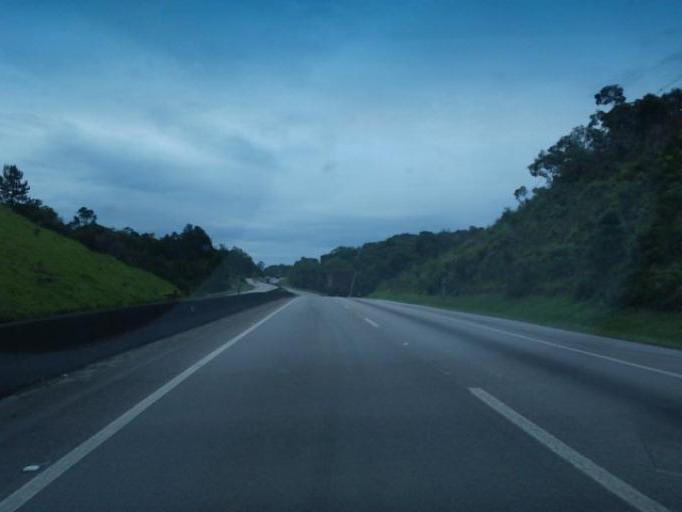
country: BR
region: Sao Paulo
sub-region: Juquitiba
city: Juquitiba
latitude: -23.9567
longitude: -47.1122
